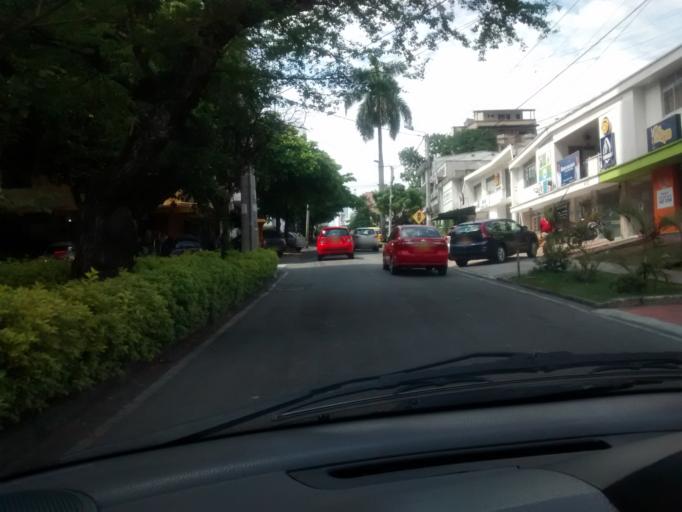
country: CO
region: Santander
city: Bucaramanga
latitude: 7.1206
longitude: -73.1095
